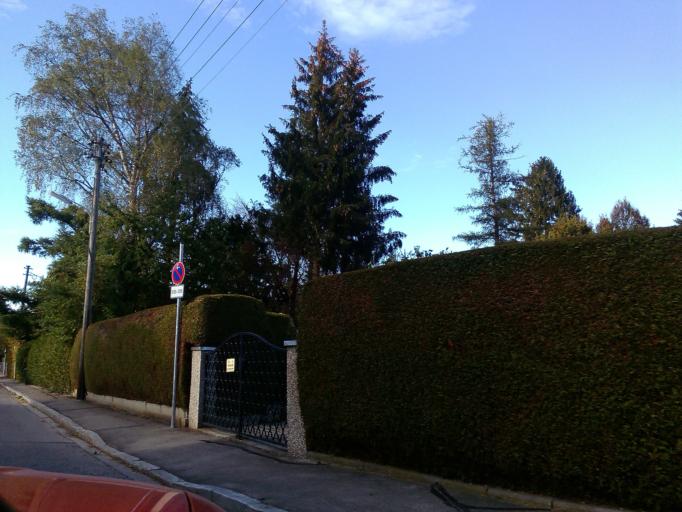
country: DE
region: Bavaria
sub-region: Upper Bavaria
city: Gauting
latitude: 48.0605
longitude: 11.3769
